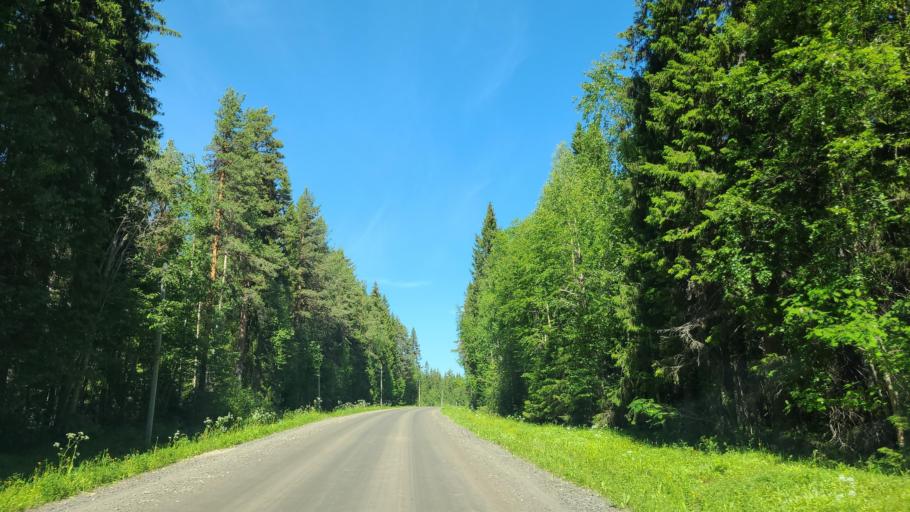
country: SE
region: Vaesterbotten
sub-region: Bjurholms Kommun
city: Bjurholm
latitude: 63.7002
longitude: 18.8981
